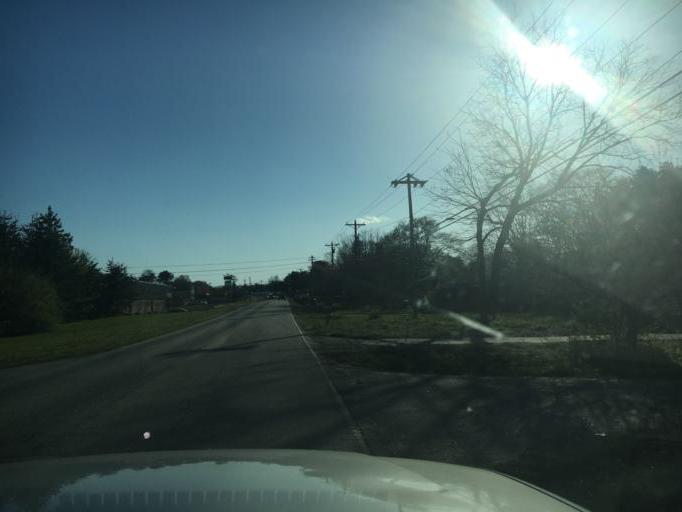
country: US
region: South Carolina
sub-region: Greenville County
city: Five Forks
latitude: 34.8393
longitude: -82.2766
